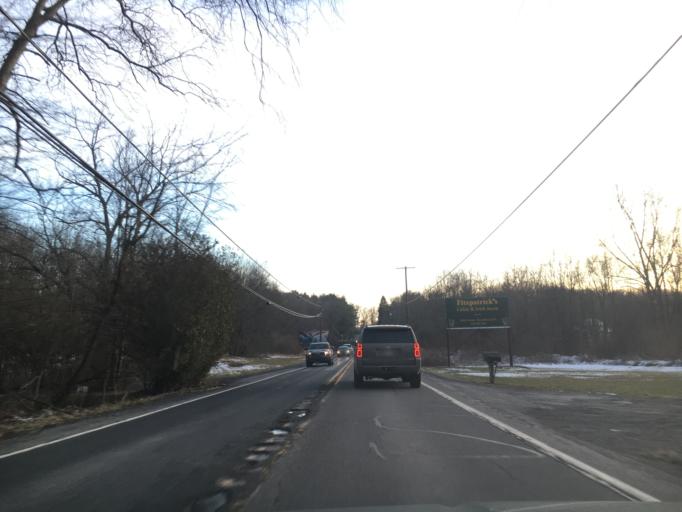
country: US
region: Pennsylvania
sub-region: Pike County
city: Saw Creek
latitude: 41.0655
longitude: -75.1149
